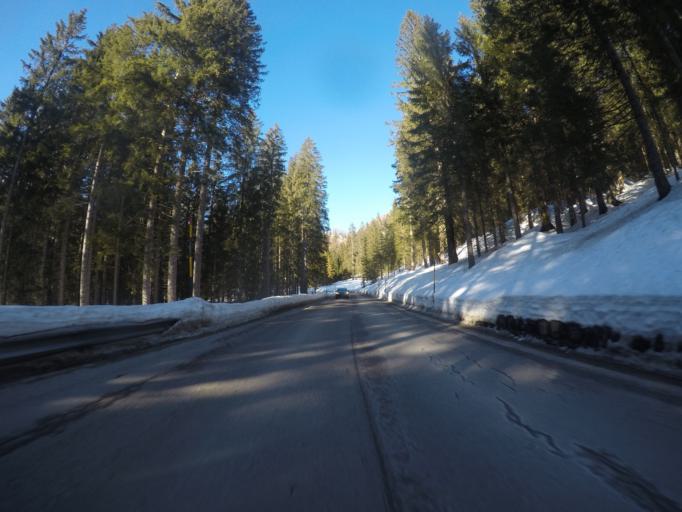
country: IT
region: Trentino-Alto Adige
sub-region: Provincia di Trento
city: Siror
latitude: 46.2681
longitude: 11.8043
